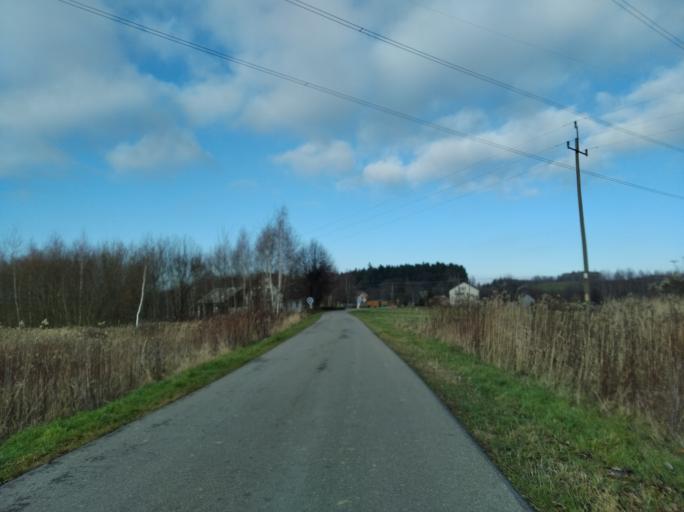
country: PL
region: Subcarpathian Voivodeship
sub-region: Powiat strzyzowski
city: Babica
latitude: 49.9041
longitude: 21.8509
